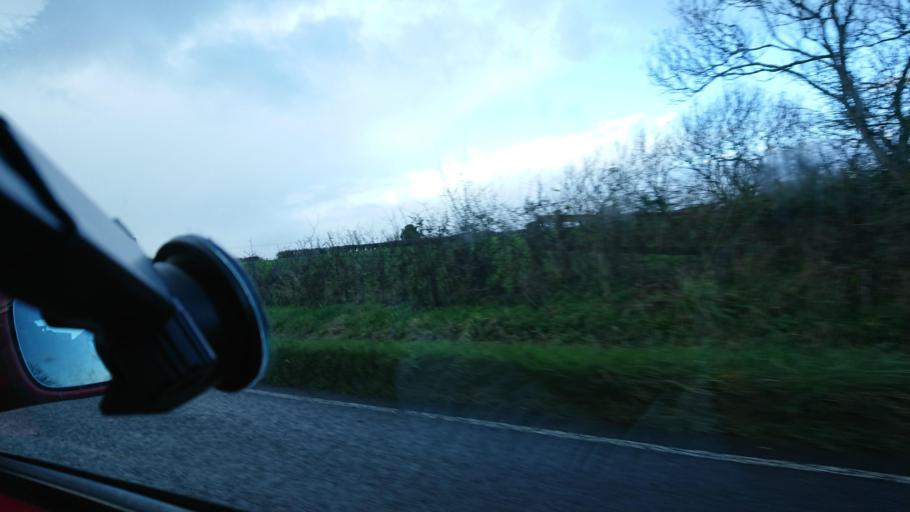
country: GB
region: England
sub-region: Cornwall
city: Looe
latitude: 50.3489
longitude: -4.4779
